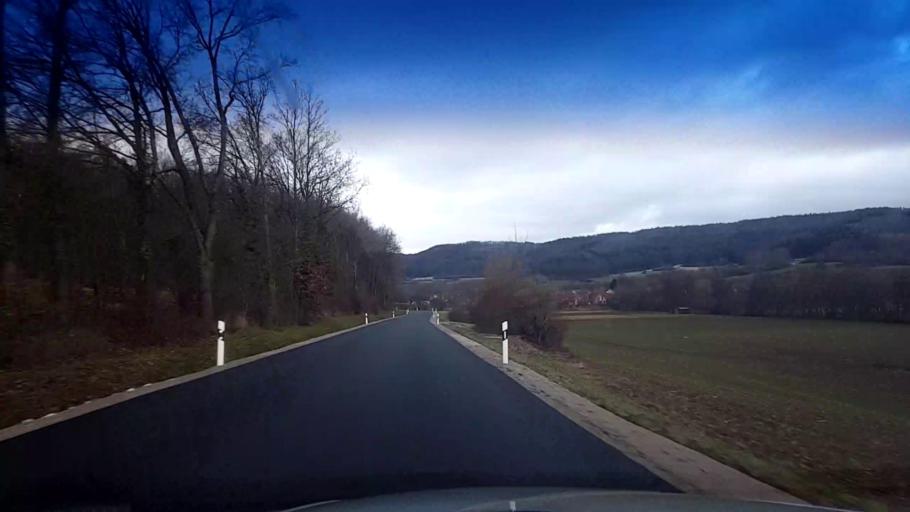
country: DE
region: Bavaria
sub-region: Upper Franconia
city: Eggolsheim
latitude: 49.8129
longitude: 11.0769
